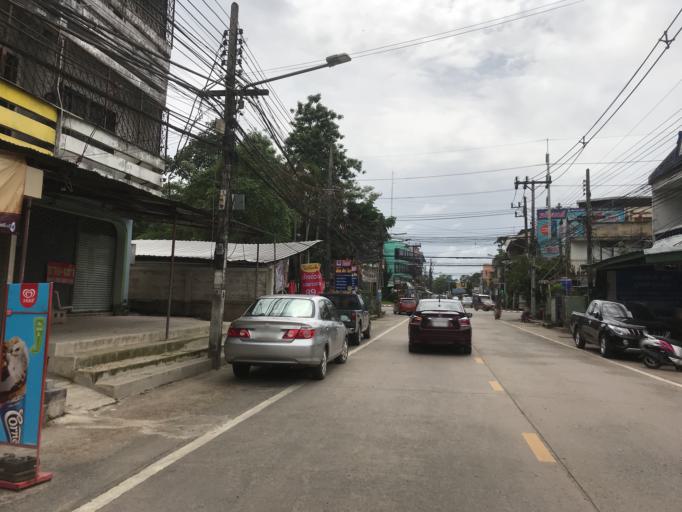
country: TH
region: Chiang Rai
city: Chiang Rai
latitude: 19.9026
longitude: 99.8159
